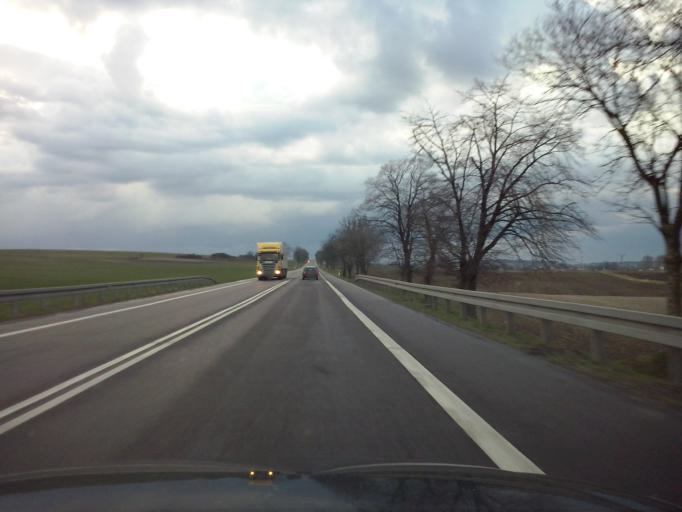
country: PL
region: Lublin Voivodeship
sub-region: Chelm
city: Chelm
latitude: 51.1661
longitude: 23.3729
